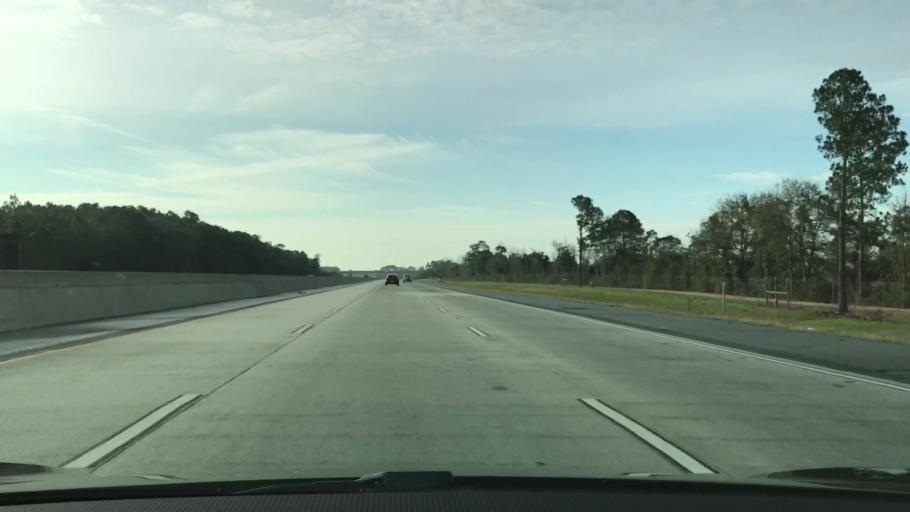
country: US
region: Georgia
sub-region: Tift County
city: Omega
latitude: 31.3011
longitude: -83.4779
